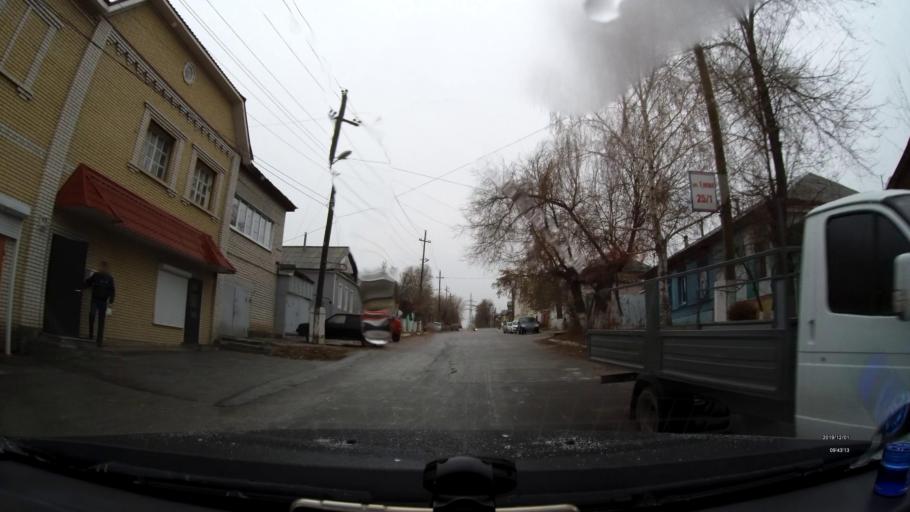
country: RU
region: Saratov
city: Vol'sk
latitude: 52.0436
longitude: 47.3826
